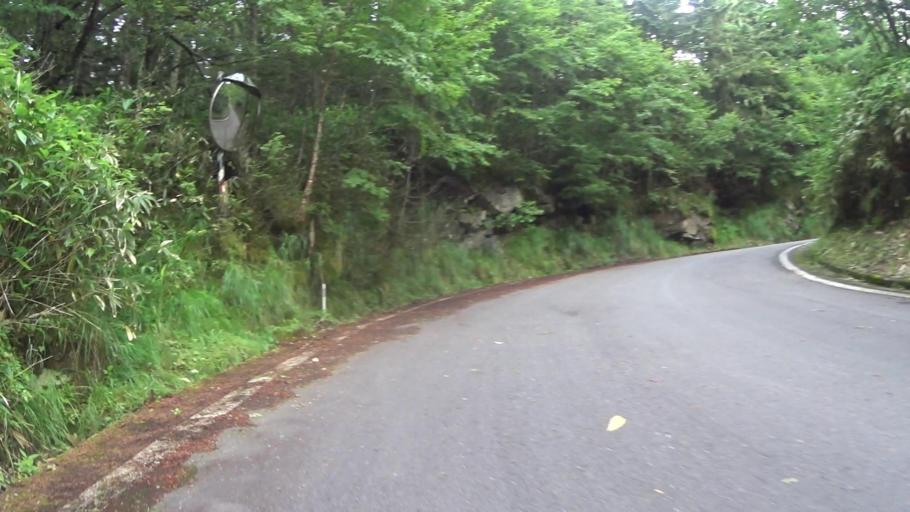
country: JP
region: Nagano
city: Saku
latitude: 36.1136
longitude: 138.3309
